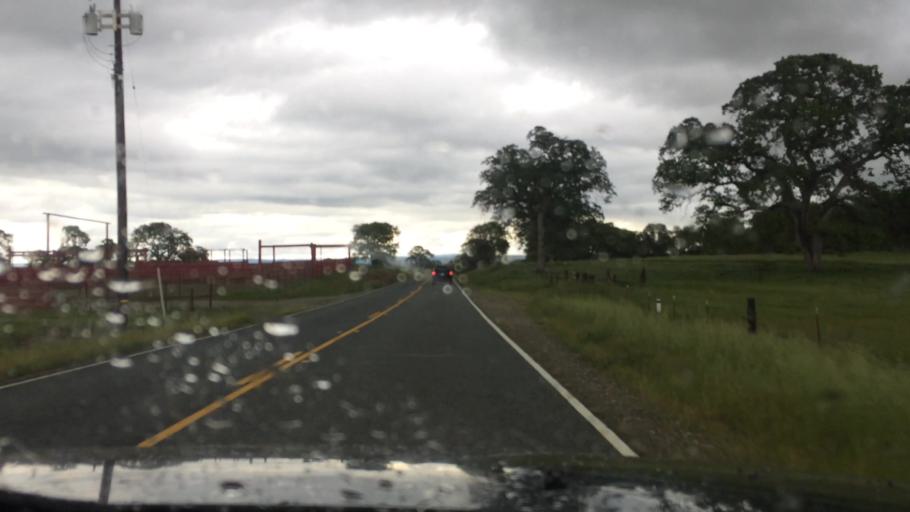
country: US
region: California
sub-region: Amador County
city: Ione
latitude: 38.3860
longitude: -121.0439
